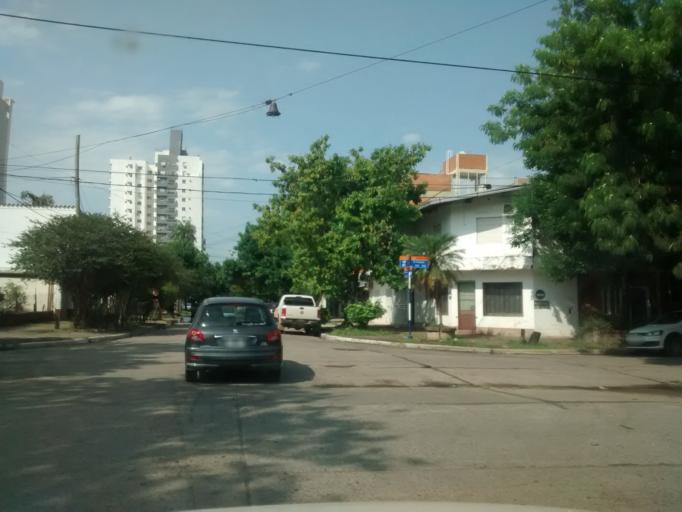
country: AR
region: Chaco
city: Resistencia
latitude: -27.4526
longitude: -58.9759
